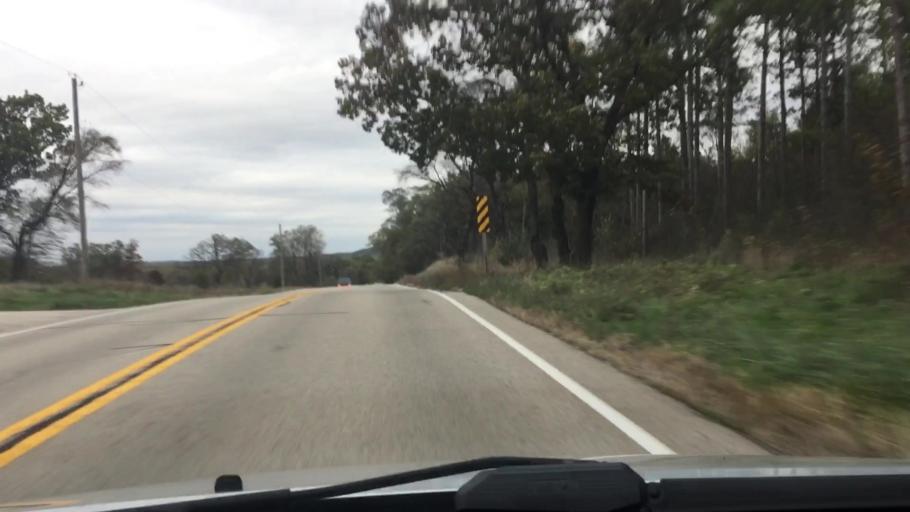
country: US
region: Wisconsin
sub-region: Waukesha County
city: Eagle
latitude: 42.9093
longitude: -88.4738
